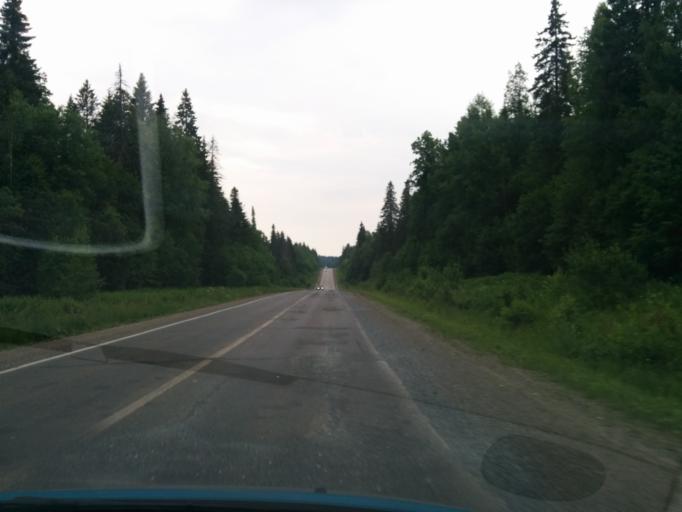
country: RU
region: Perm
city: Perm
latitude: 58.1891
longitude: 56.2167
